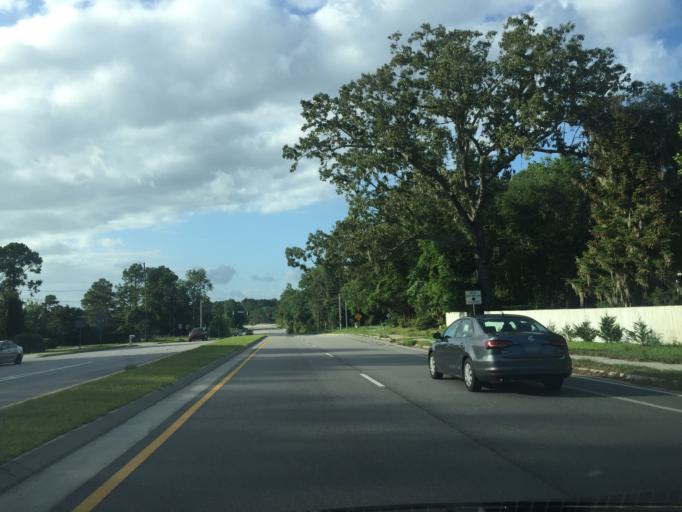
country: US
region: Georgia
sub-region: Chatham County
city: Isle of Hope
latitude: 31.9845
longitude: -81.1051
